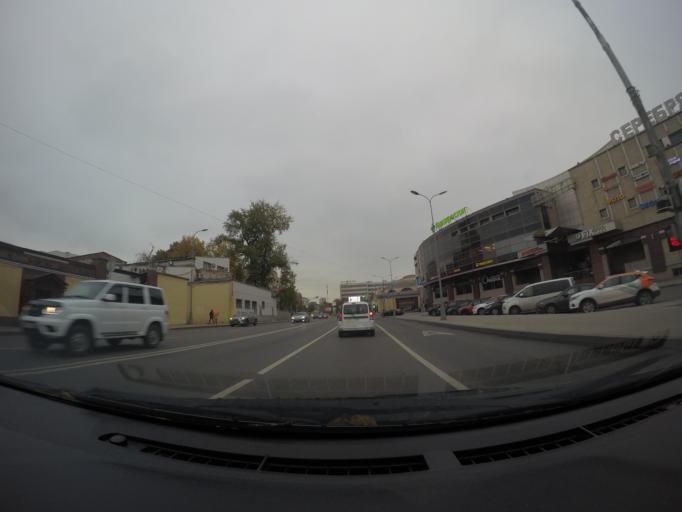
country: RU
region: Moscow
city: Lefortovo
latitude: 55.7826
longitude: 37.7035
